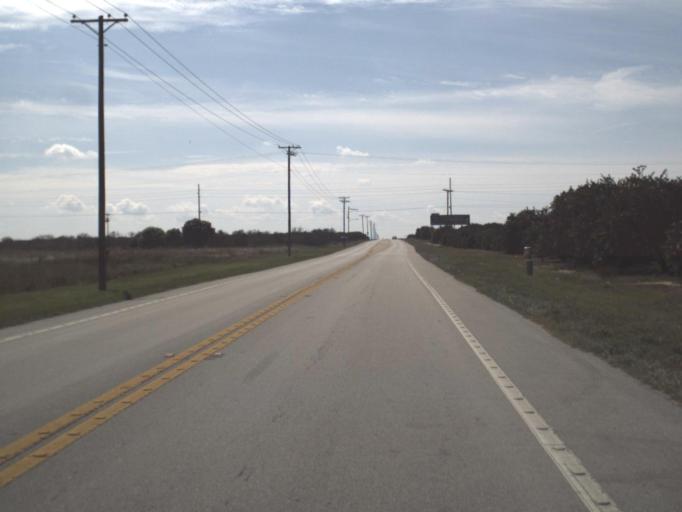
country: US
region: Florida
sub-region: Highlands County
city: Sebring
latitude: 27.5361
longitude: -81.4534
